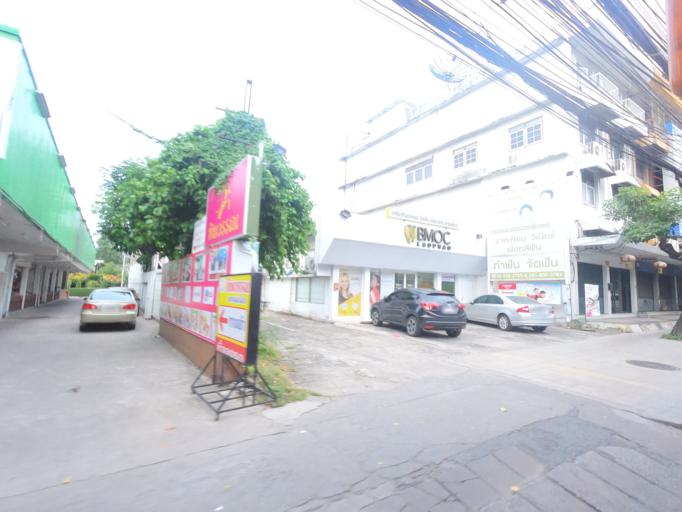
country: TH
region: Bangkok
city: Wang Thonglang
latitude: 13.7763
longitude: 100.6271
